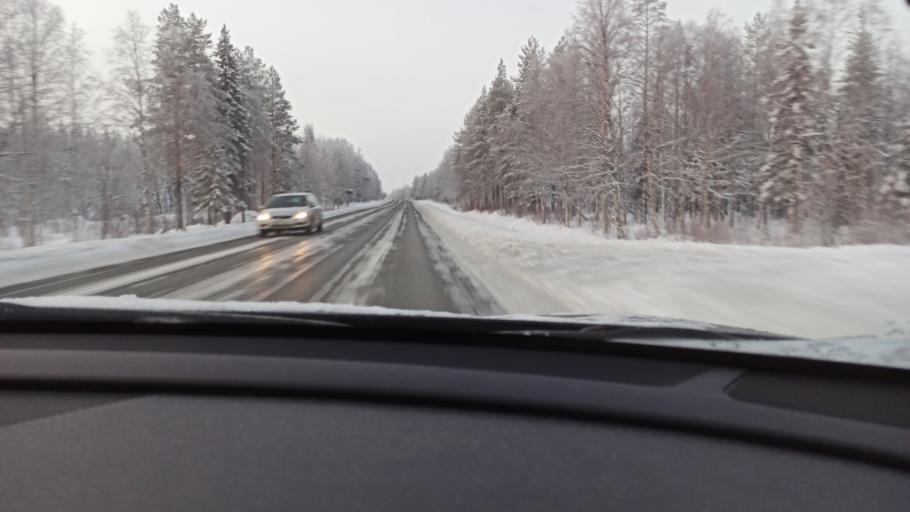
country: FI
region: Lapland
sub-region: Rovaniemi
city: Rovaniemi
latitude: 66.5485
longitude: 25.8743
